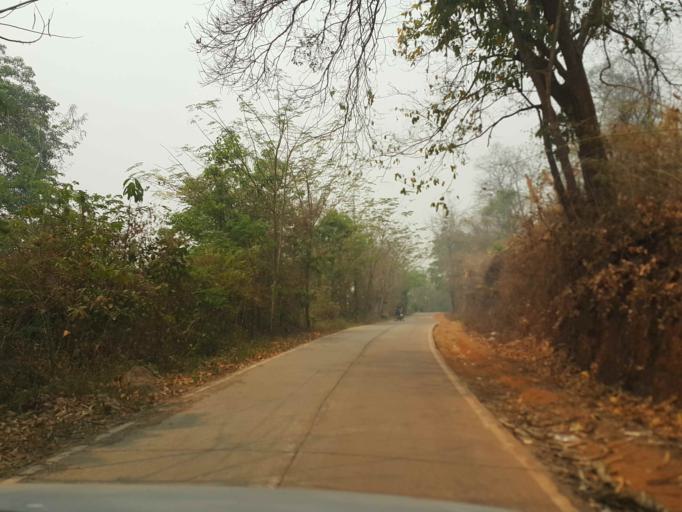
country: TH
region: Chiang Mai
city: Mae Taeng
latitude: 19.2158
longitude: 98.8644
